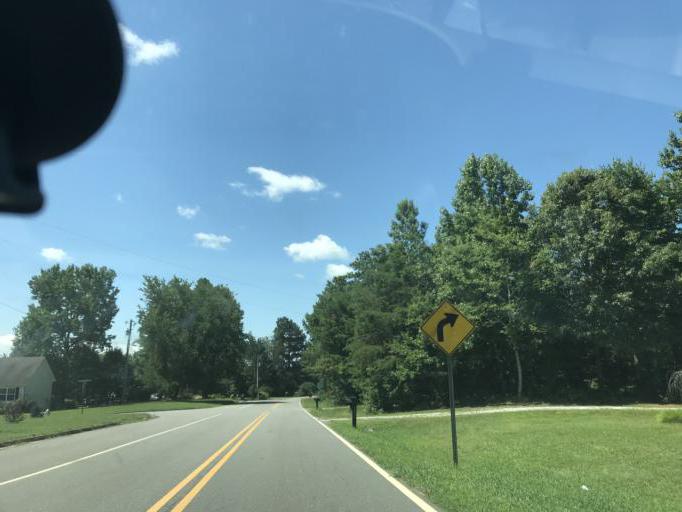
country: US
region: Georgia
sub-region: Dawson County
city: Dawsonville
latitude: 34.3149
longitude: -84.0193
